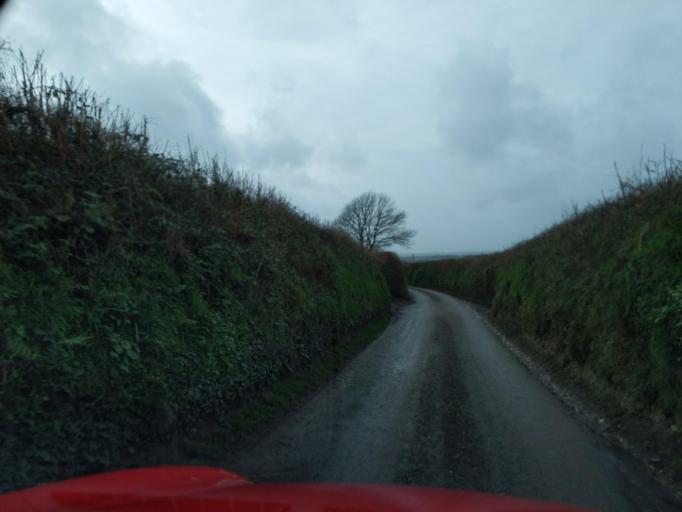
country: GB
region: England
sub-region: Cornwall
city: Fowey
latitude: 50.3428
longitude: -4.5703
